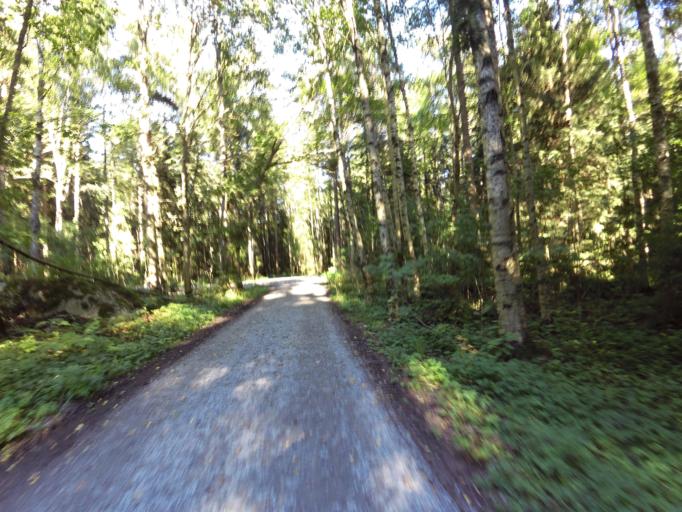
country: FI
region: Pirkanmaa
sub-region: Tampere
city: Yloejaervi
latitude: 61.5067
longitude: 23.6086
